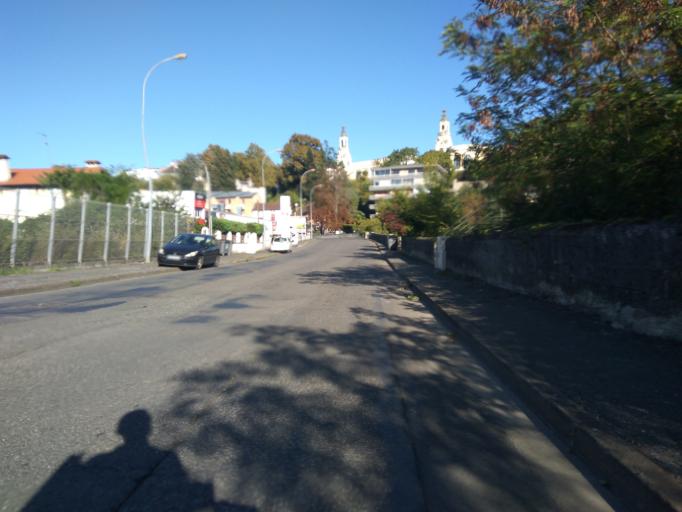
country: FR
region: Aquitaine
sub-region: Departement des Pyrenees-Atlantiques
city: Pau
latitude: 43.2925
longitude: -0.3598
